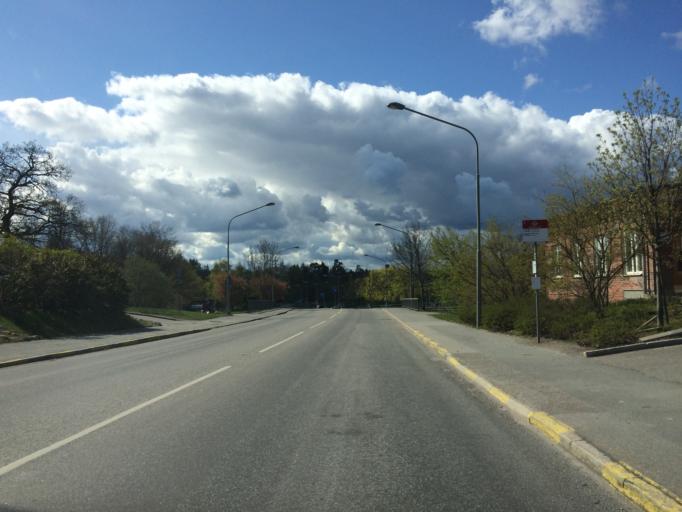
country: SE
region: Stockholm
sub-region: Huddinge Kommun
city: Segeltorp
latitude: 59.2917
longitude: 17.9316
